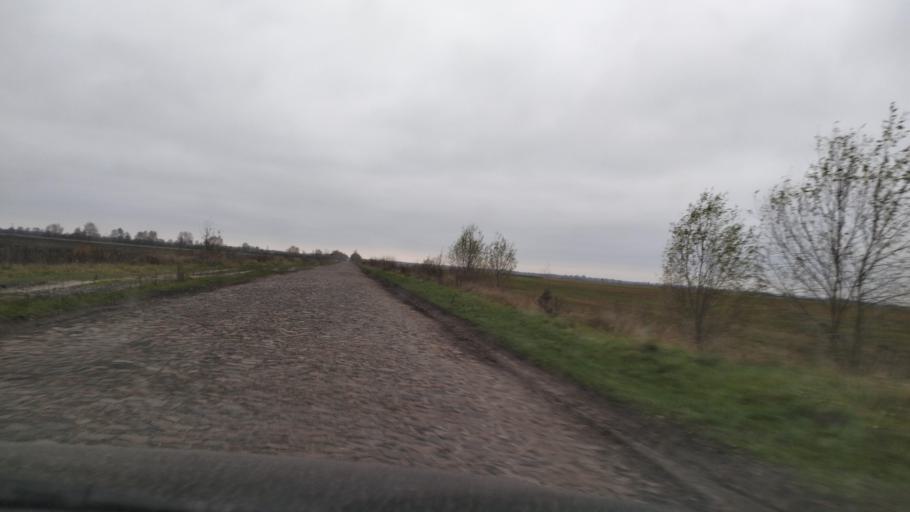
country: BY
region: Brest
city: Davyd-Haradok
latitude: 52.0090
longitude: 27.2055
